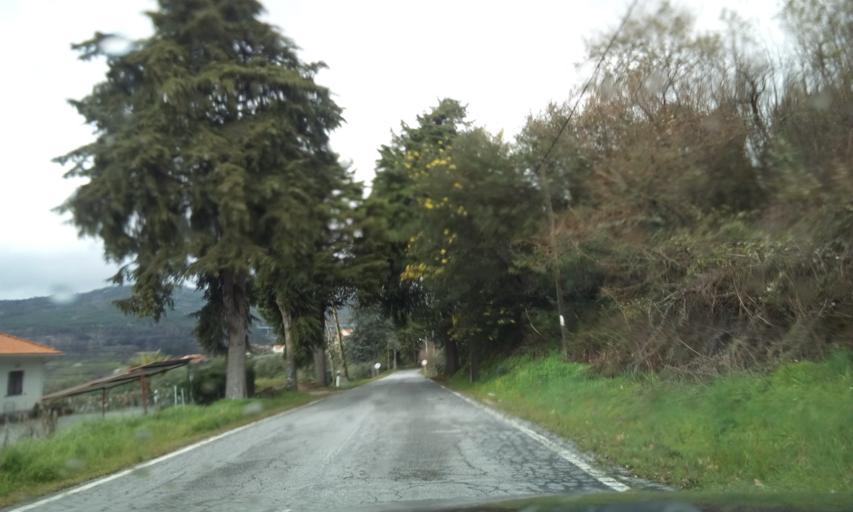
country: PT
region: Guarda
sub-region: Fornos de Algodres
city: Fornos de Algodres
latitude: 40.6111
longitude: -7.5843
